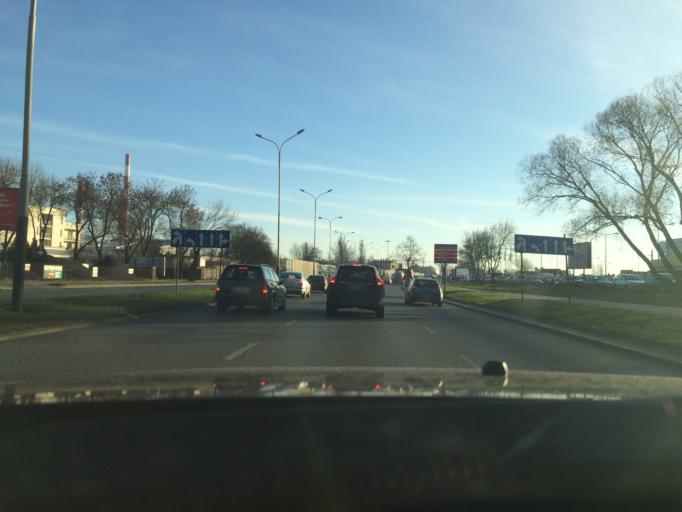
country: PL
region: Lodz Voivodeship
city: Lodz
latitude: 51.7473
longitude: 19.4390
